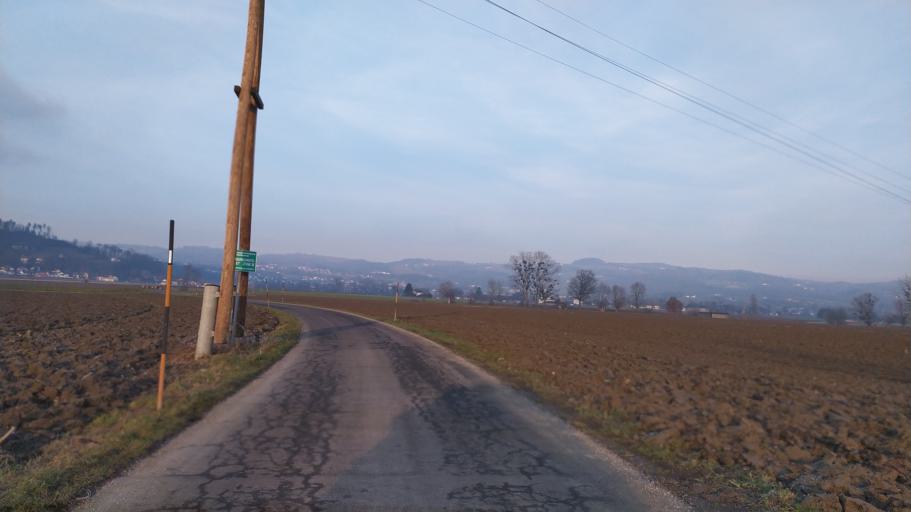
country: AT
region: Upper Austria
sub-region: Politischer Bezirk Urfahr-Umgebung
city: Walding
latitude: 48.3329
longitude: 14.1416
